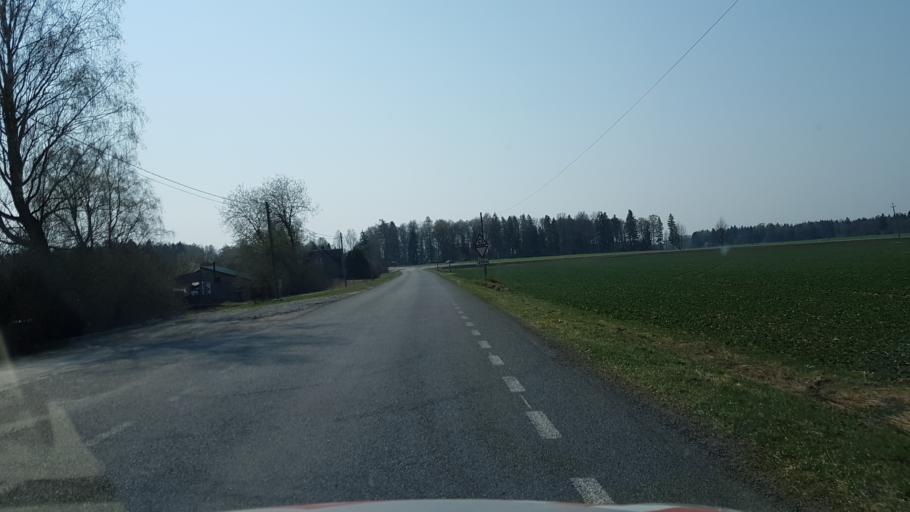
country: EE
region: Raplamaa
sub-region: Kehtna vald
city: Kehtna
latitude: 59.0579
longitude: 24.9519
